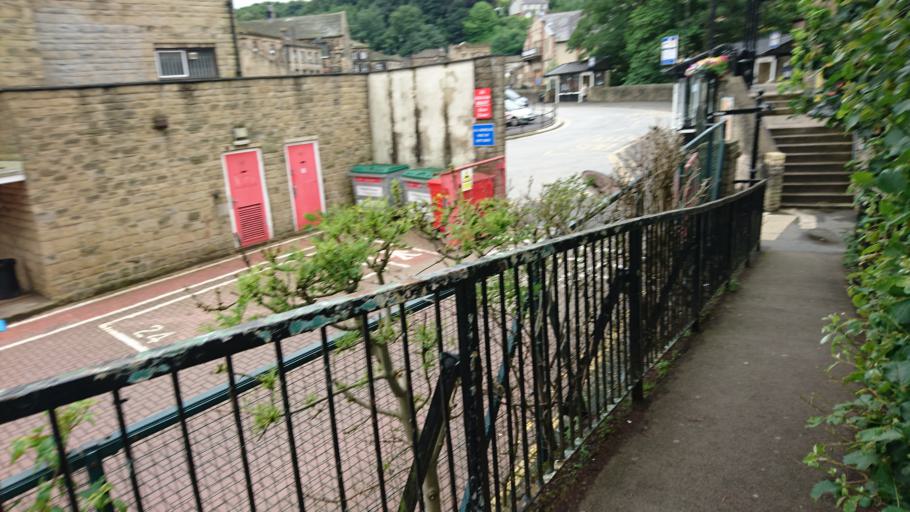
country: GB
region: England
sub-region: Kirklees
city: Holmfirth
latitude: 53.5711
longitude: -1.7862
